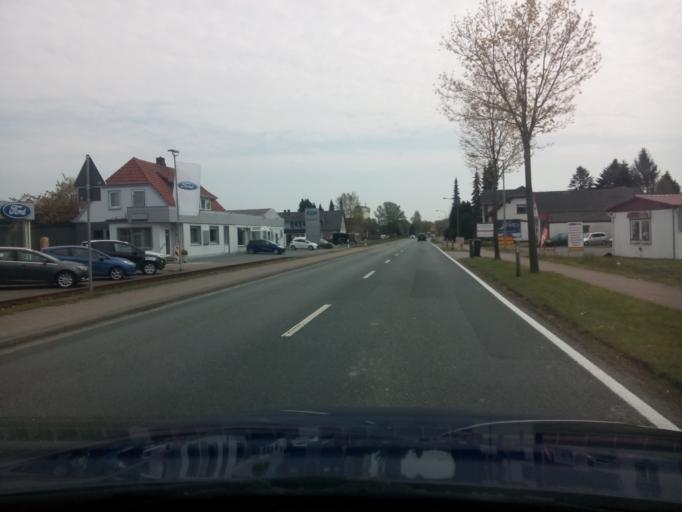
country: DE
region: Lower Saxony
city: Syke
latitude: 52.8814
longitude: 8.8611
